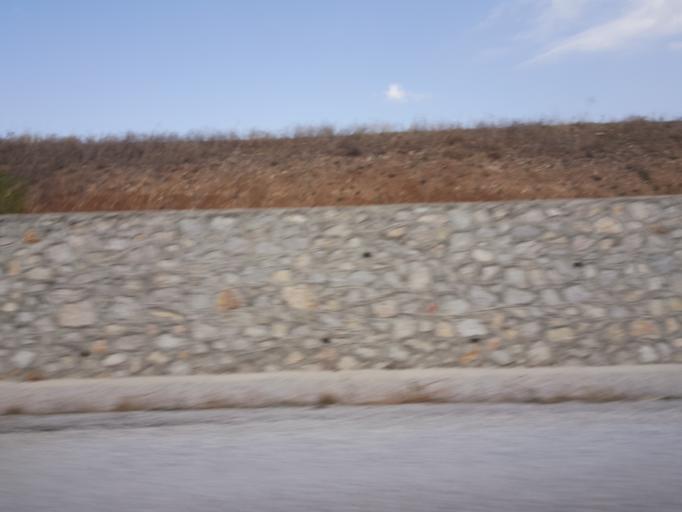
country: TR
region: Corum
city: Alaca
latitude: 40.1562
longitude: 34.7218
